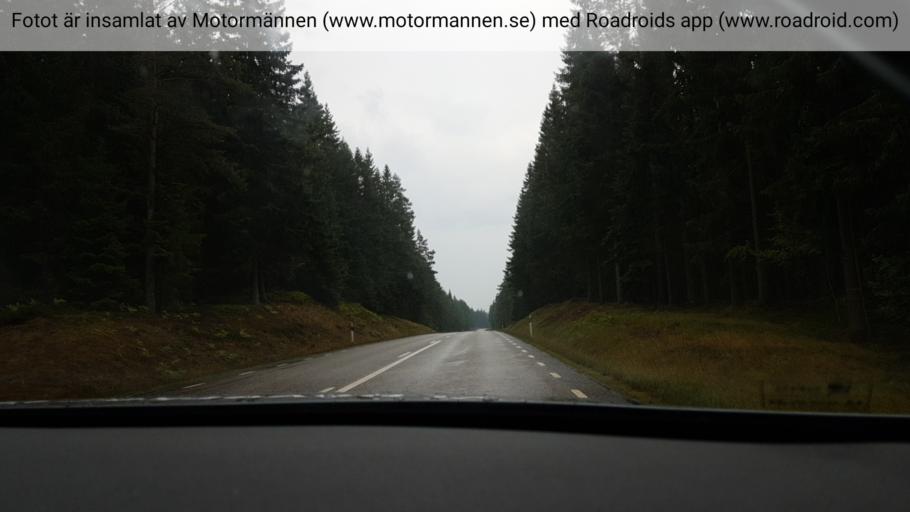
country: SE
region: Joenkoeping
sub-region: Vaggeryds Kommun
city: Vaggeryd
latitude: 57.5624
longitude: 14.2499
